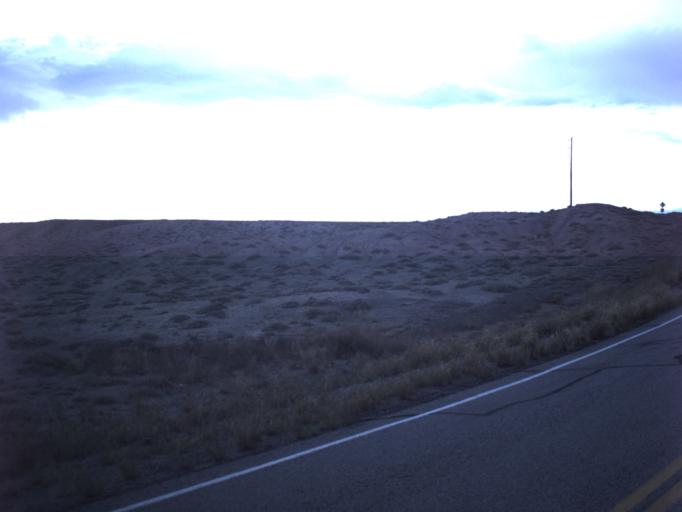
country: US
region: Utah
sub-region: Grand County
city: Moab
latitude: 38.9013
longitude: -109.3145
